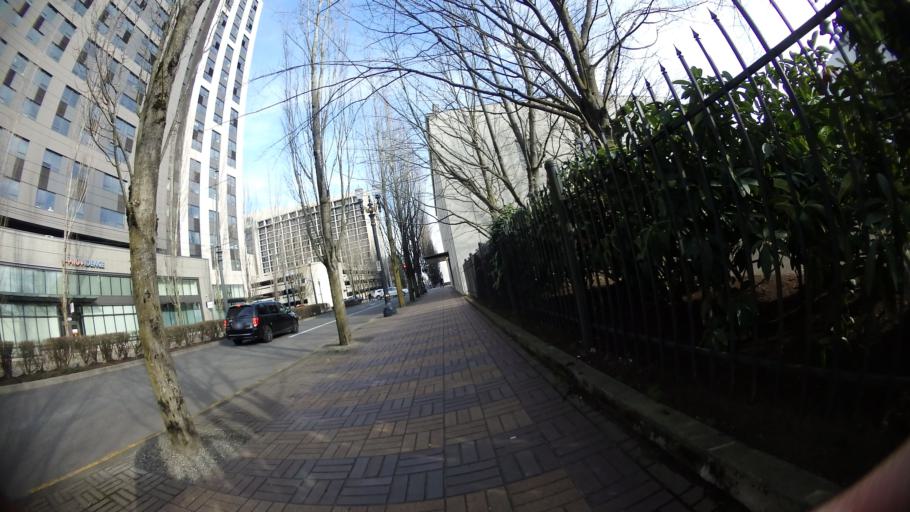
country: US
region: Oregon
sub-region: Multnomah County
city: Portland
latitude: 45.5301
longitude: -122.6577
